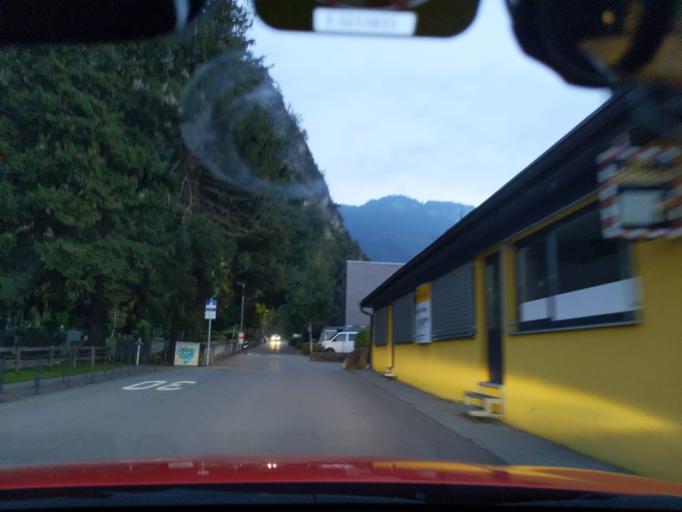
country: AT
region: Vorarlberg
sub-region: Politischer Bezirk Dornbirn
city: Hohenems
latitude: 47.3656
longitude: 9.6906
